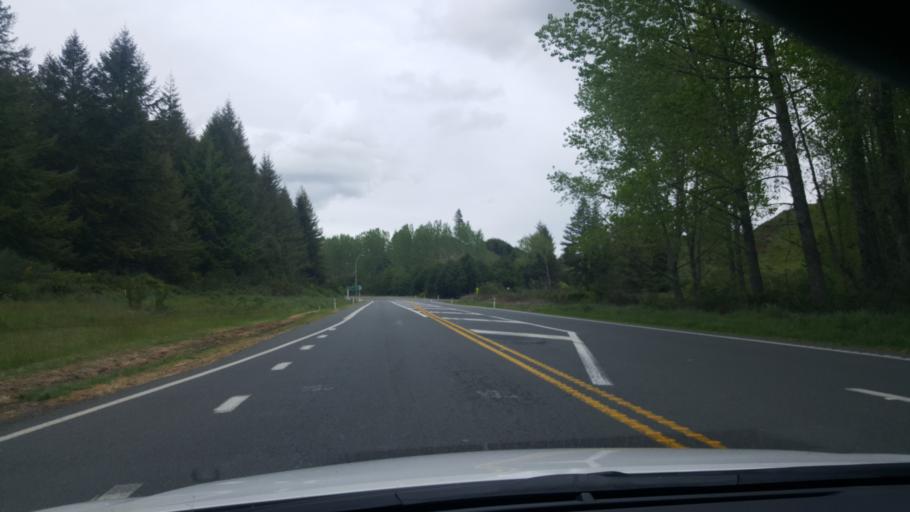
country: NZ
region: Bay of Plenty
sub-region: Rotorua District
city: Rotorua
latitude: -38.2250
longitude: 176.2900
